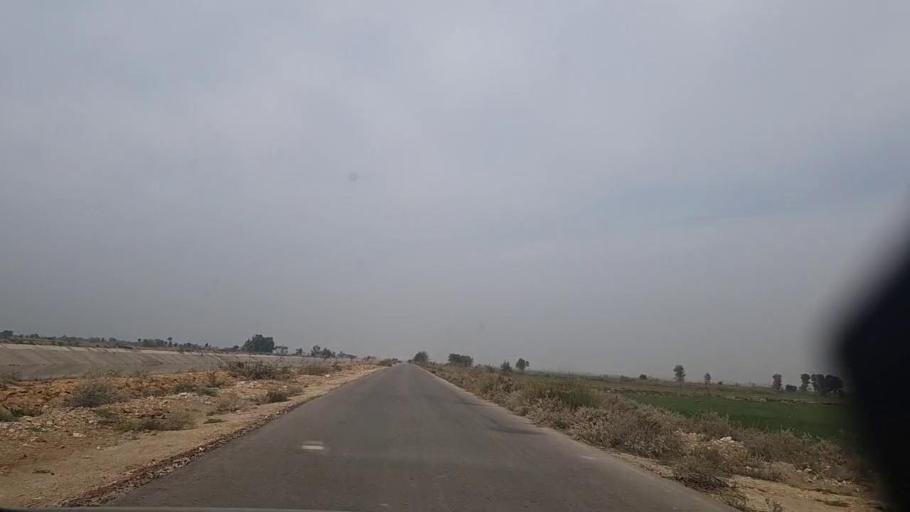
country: PK
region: Sindh
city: Sakrand
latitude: 26.2556
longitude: 68.2469
